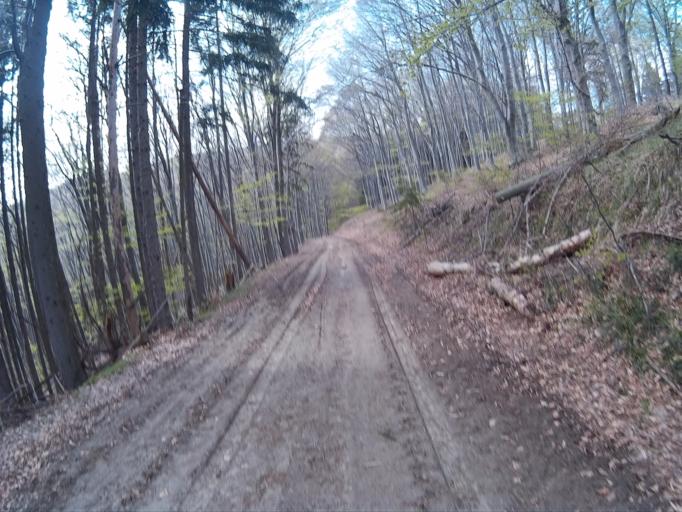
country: AT
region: Burgenland
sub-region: Politischer Bezirk Oberwart
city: Rechnitz
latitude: 47.3486
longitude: 16.4468
